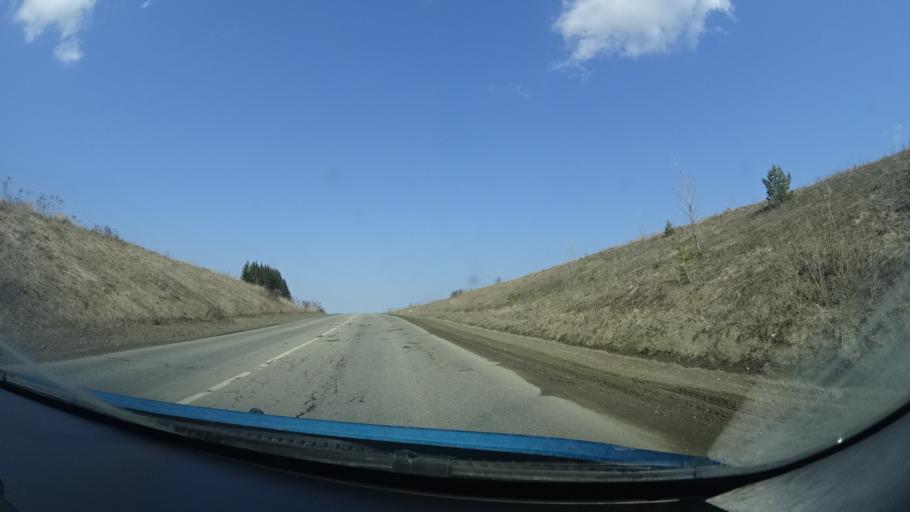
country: RU
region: Perm
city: Osa
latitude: 57.2613
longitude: 55.5756
